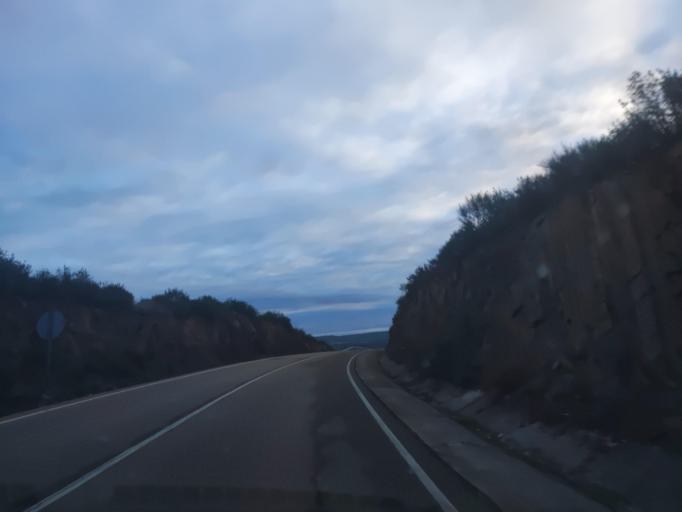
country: ES
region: Castille and Leon
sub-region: Provincia de Salamanca
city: Castillejo de Martin Viejo
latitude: 40.7047
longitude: -6.6476
